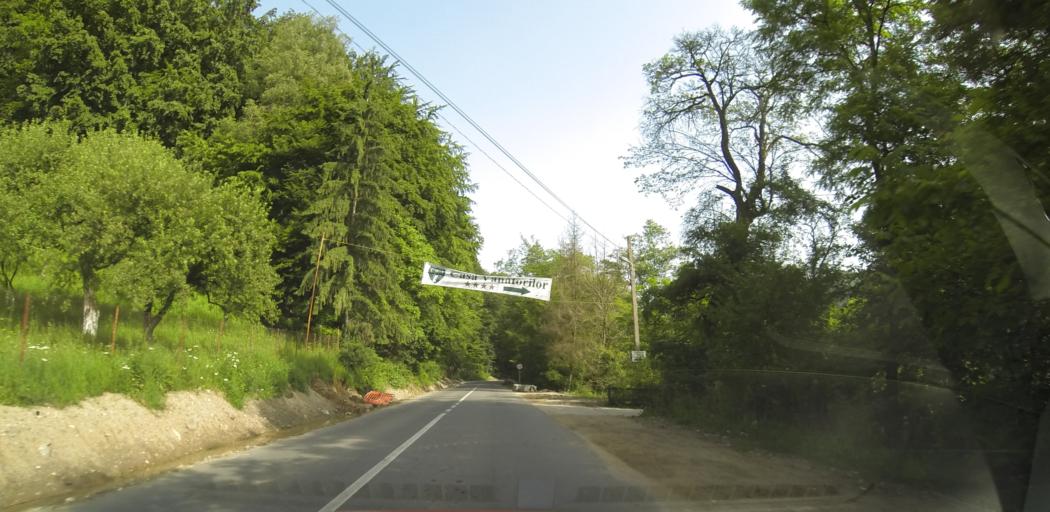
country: RO
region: Valcea
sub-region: Oras Baile Olanesti
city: Olanesti
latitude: 45.1936
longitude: 24.2510
